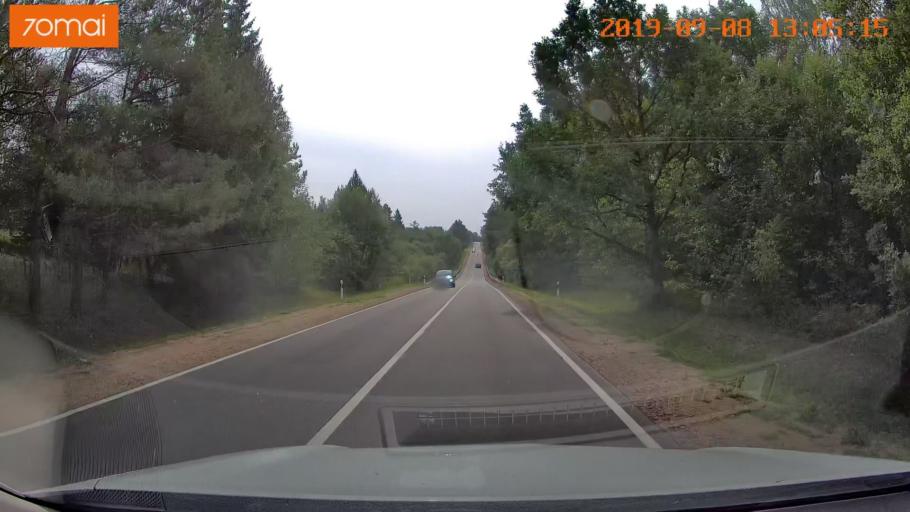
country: LT
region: Kauno apskritis
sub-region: Kauno rajonas
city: Karmelava
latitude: 54.8559
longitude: 24.2362
